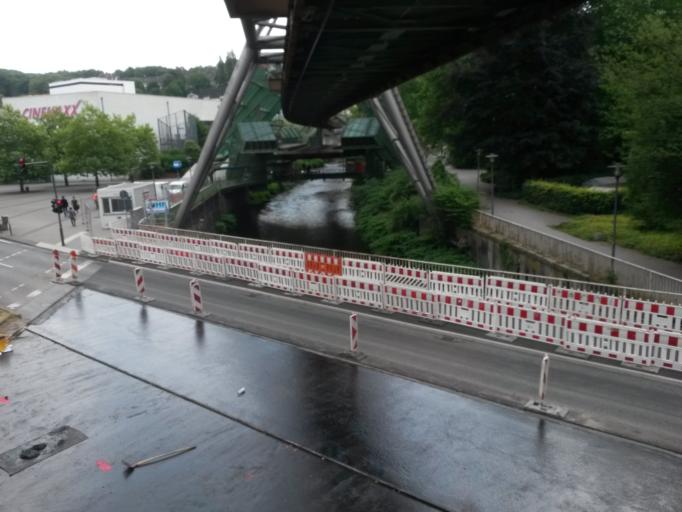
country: DE
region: North Rhine-Westphalia
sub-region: Regierungsbezirk Dusseldorf
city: Wuppertal
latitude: 51.2559
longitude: 7.1541
